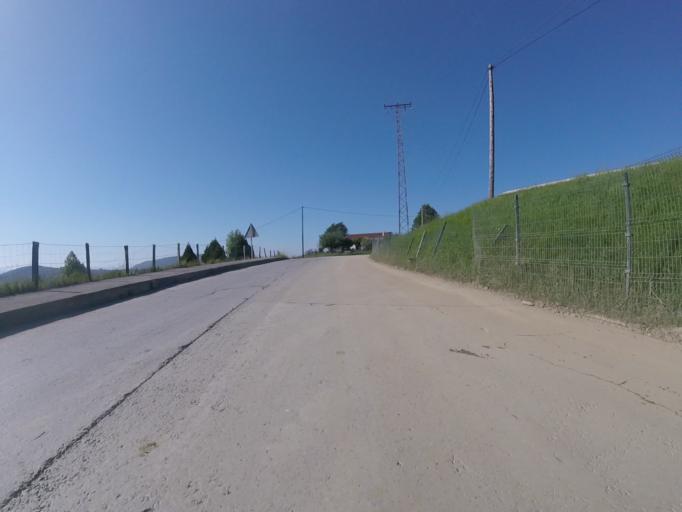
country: ES
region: Basque Country
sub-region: Provincia de Guipuzcoa
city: Astigarraga
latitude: 43.2988
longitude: -1.9342
